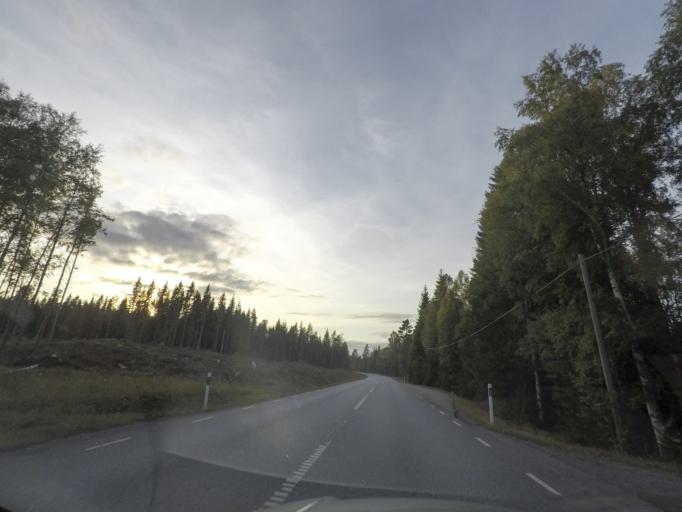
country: SE
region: OErebro
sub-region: Nora Kommun
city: As
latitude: 59.5517
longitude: 14.7553
